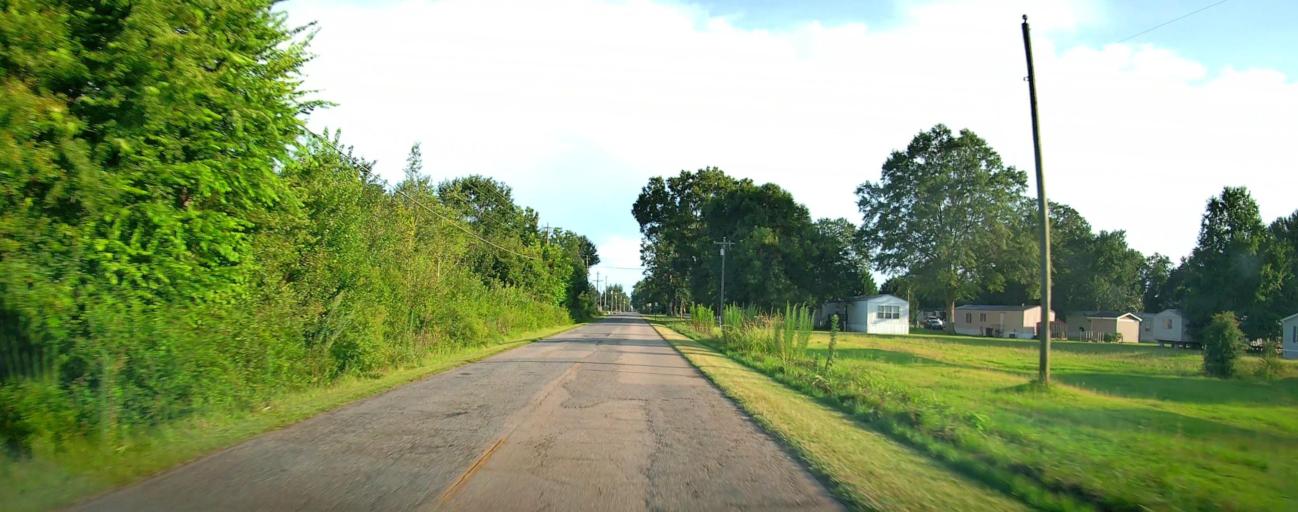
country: US
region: Georgia
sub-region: Peach County
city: Fort Valley
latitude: 32.5735
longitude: -83.8738
